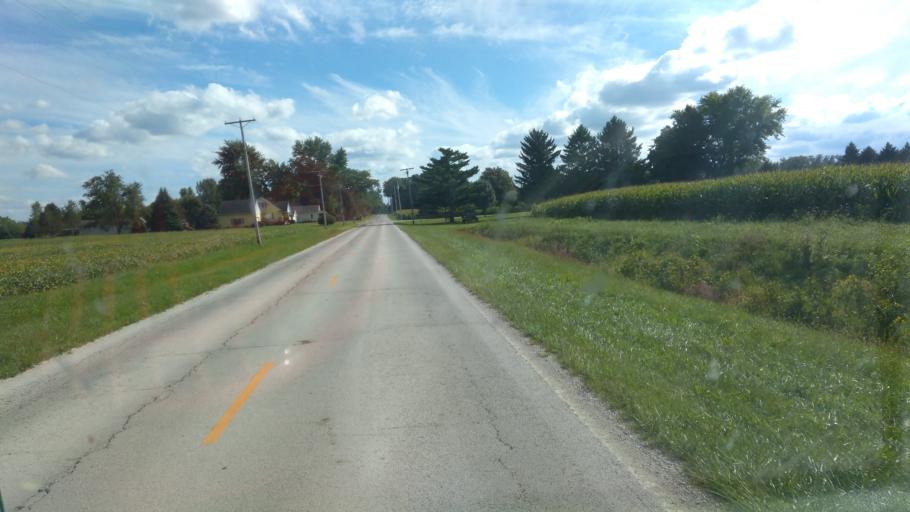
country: US
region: Ohio
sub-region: Sandusky County
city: Clyde
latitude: 41.3034
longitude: -83.0088
